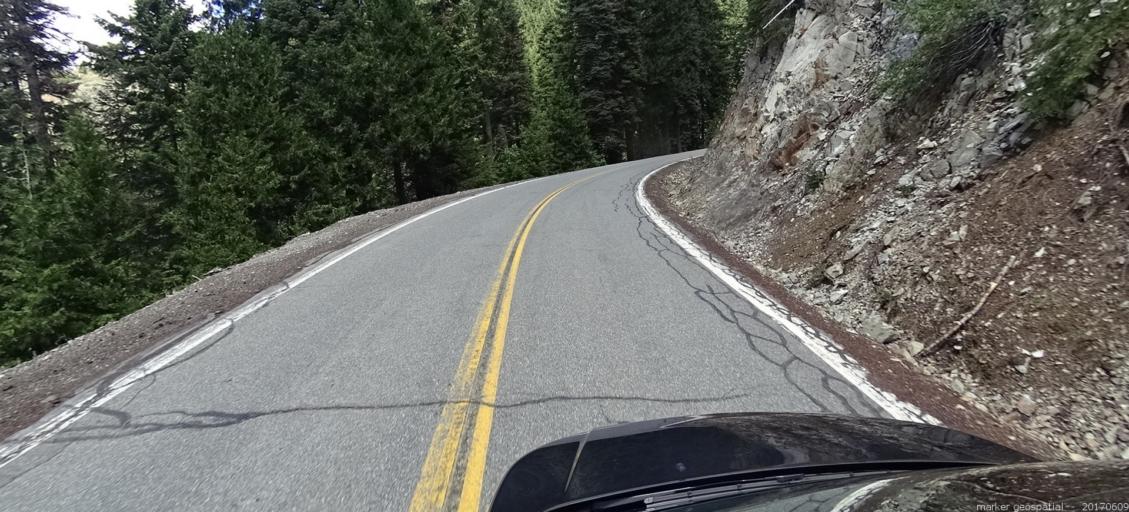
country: US
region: California
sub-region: Siskiyou County
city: Yreka
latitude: 41.3866
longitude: -122.9938
